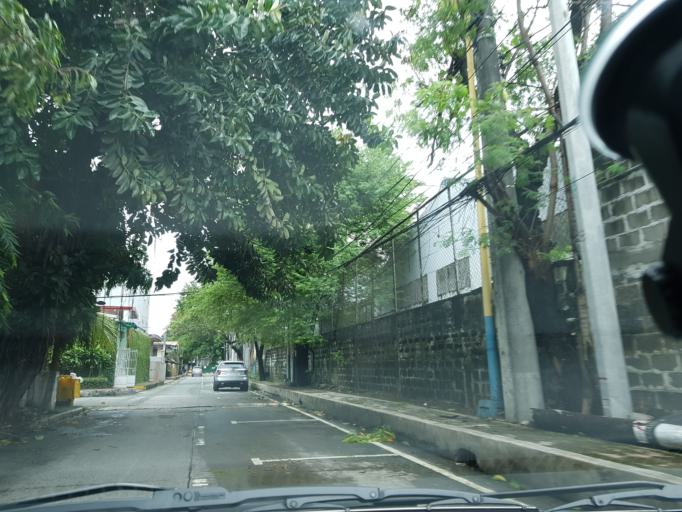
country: PH
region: Metro Manila
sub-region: Pasig
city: Pasig City
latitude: 14.5690
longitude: 121.0698
